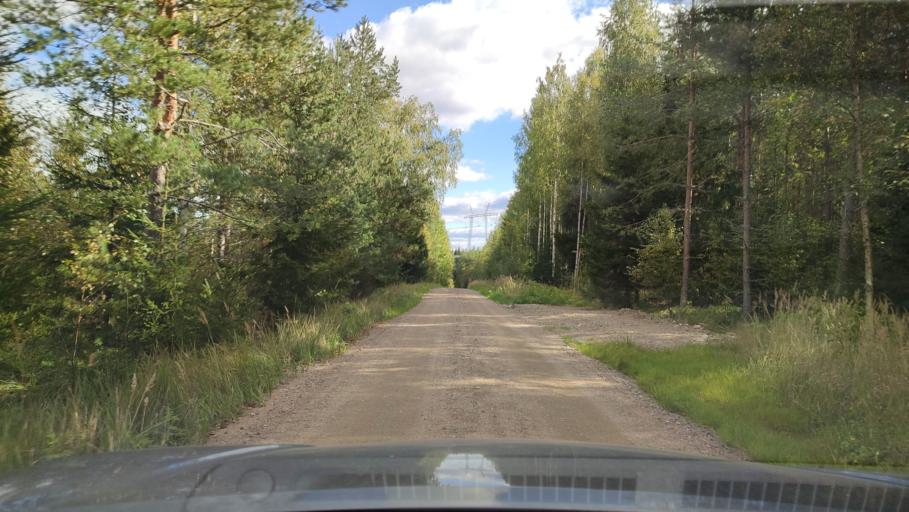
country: FI
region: Southern Ostrobothnia
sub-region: Suupohja
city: Karijoki
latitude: 62.2162
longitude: 21.6235
